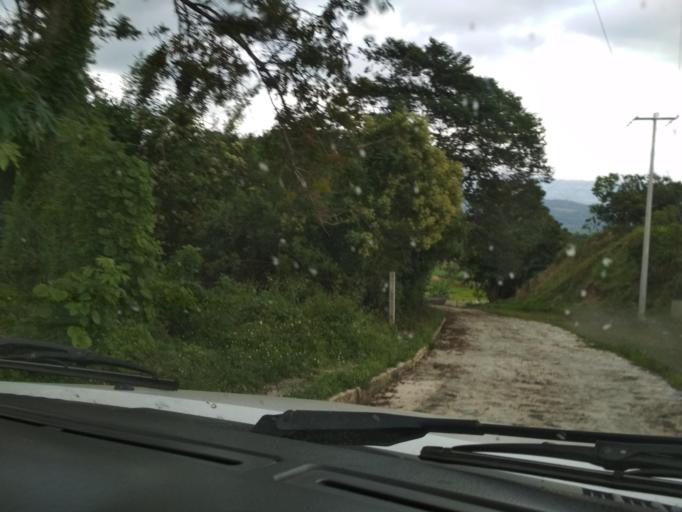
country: MX
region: Veracruz
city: El Castillo
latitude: 19.5696
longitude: -96.8319
